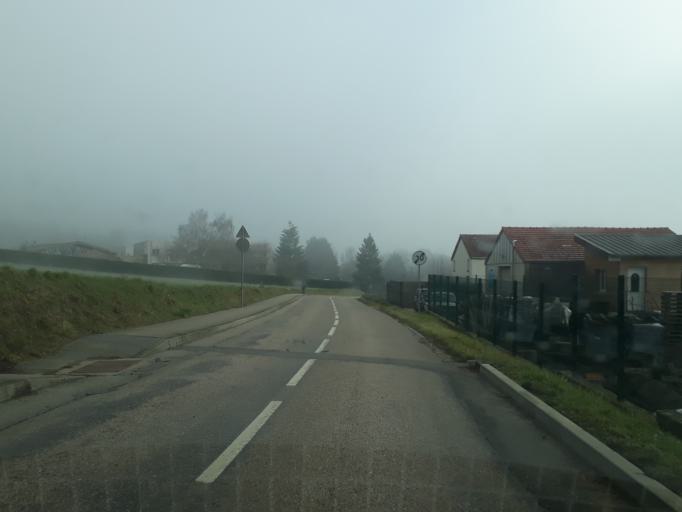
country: FR
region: Lorraine
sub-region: Departement de Meurthe-et-Moselle
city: Bouxieres-aux-Dames
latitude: 48.7470
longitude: 6.1795
